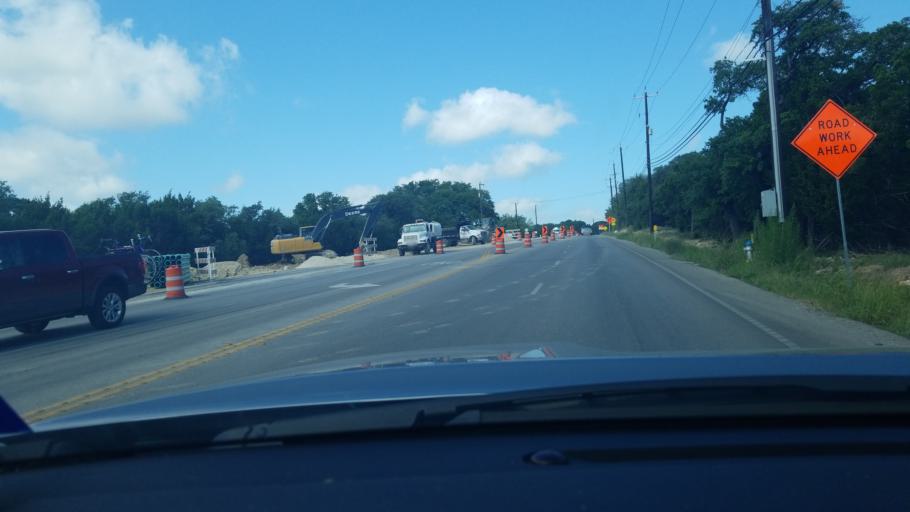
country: US
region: Texas
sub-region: Bexar County
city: Timberwood Park
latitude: 29.7095
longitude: -98.4845
